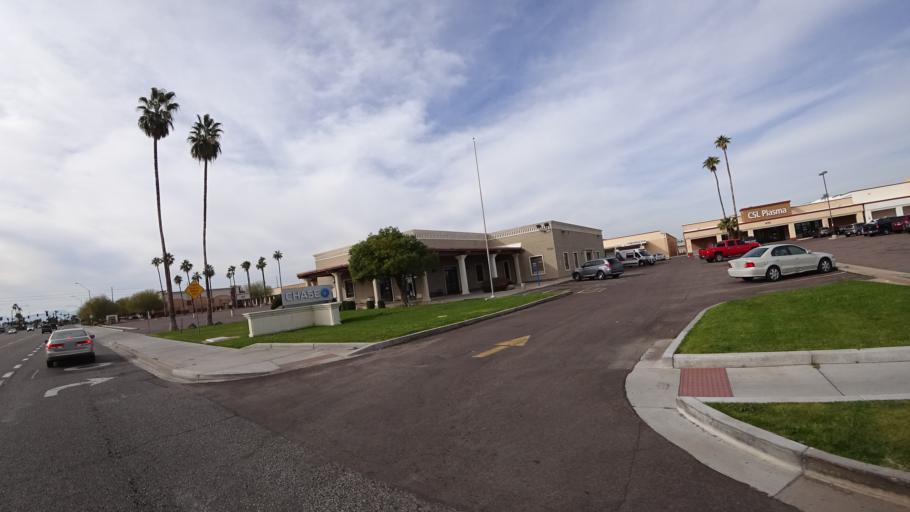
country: US
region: Arizona
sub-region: Maricopa County
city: Sun City
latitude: 33.5805
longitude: -112.2700
